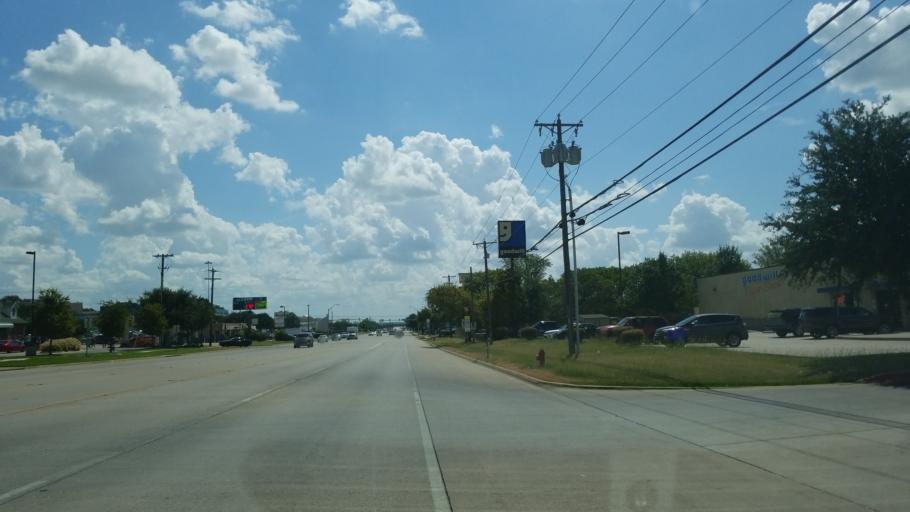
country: US
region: Texas
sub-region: Tarrant County
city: Euless
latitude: 32.8464
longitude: -97.1000
